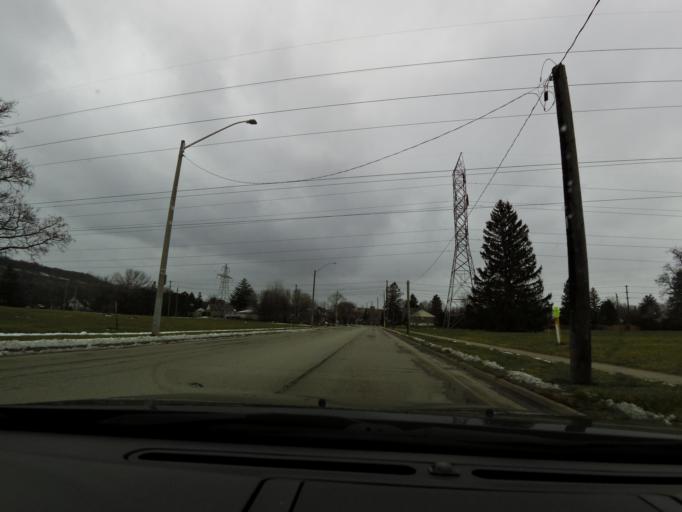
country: CA
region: Ontario
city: Ancaster
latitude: 43.2525
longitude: -79.9320
